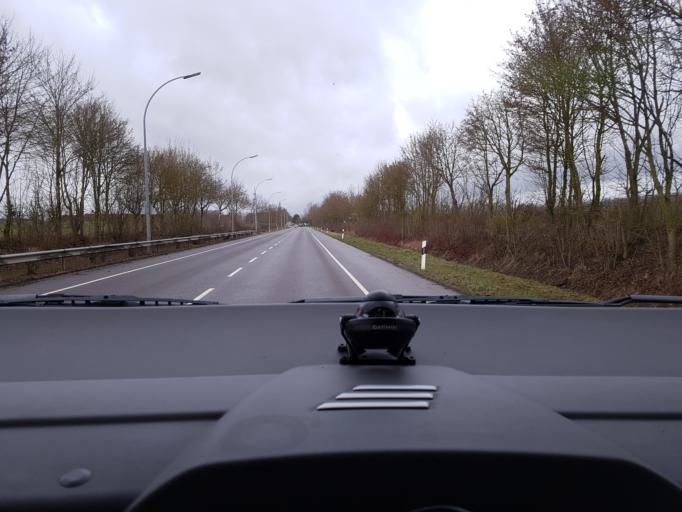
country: LU
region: Luxembourg
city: Capellen
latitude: 49.6462
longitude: 5.9715
